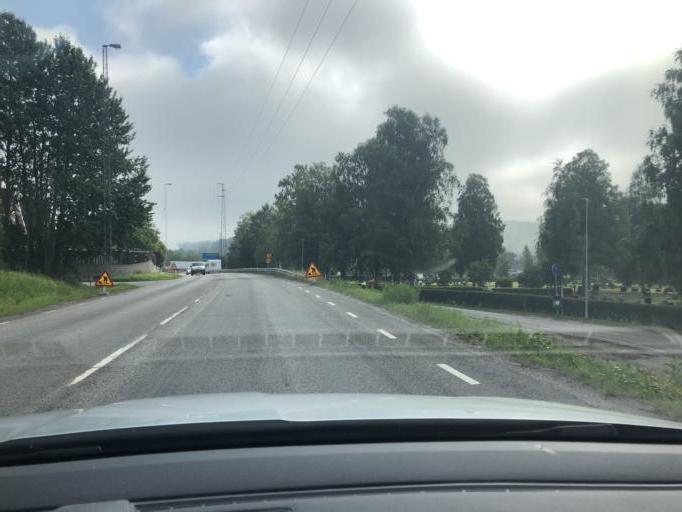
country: SE
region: Vaesternorrland
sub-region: Sundsvalls Kommun
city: Sundsvall
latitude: 62.4108
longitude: 17.3282
